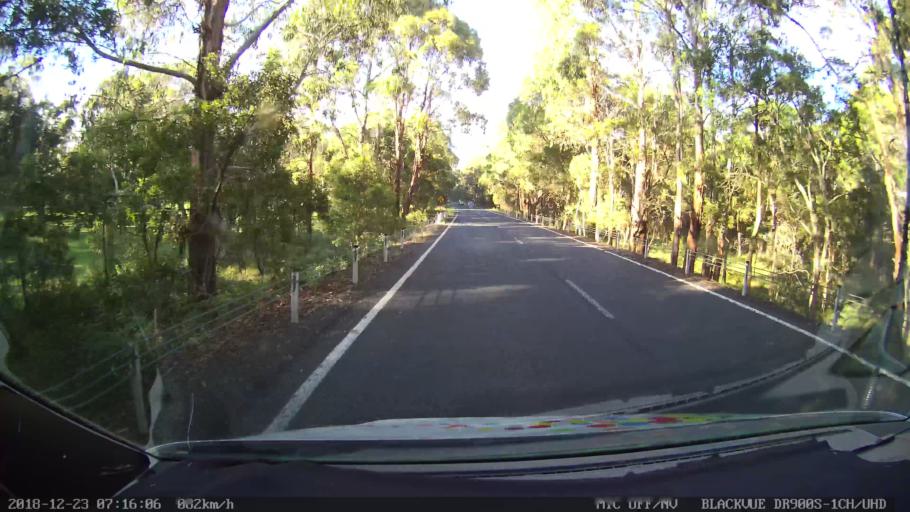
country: AU
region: New South Wales
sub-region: Bellingen
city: Dorrigo
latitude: -30.4523
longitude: 152.3120
